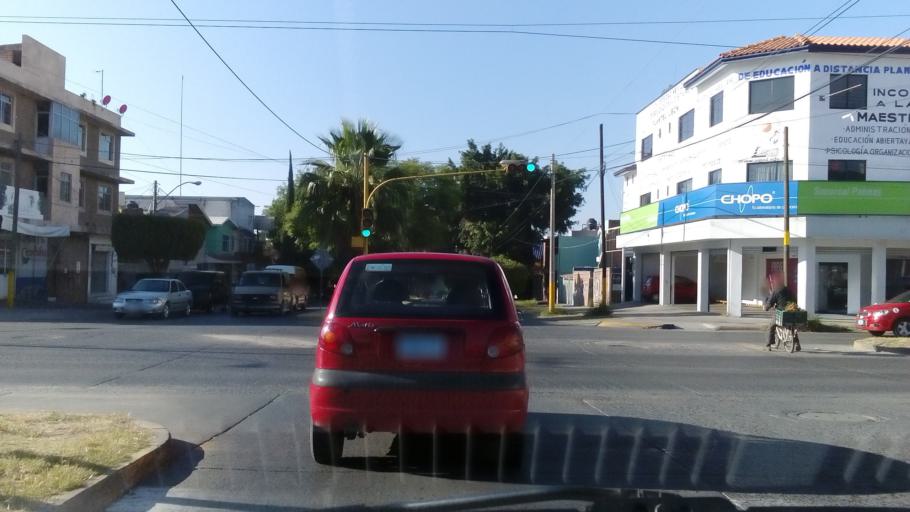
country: MX
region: Guanajuato
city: Leon
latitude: 21.1167
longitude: -101.6994
